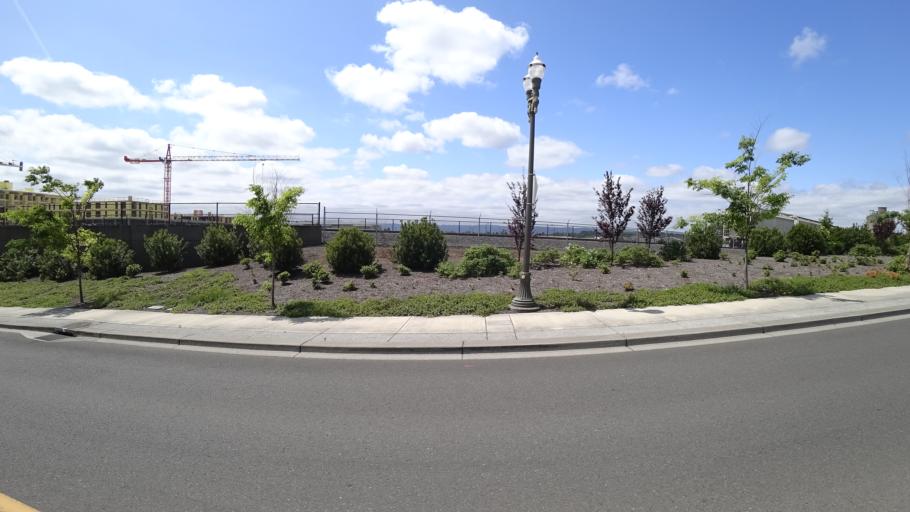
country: US
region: Washington
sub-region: Clark County
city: Vancouver
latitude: 45.6262
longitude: -122.6799
